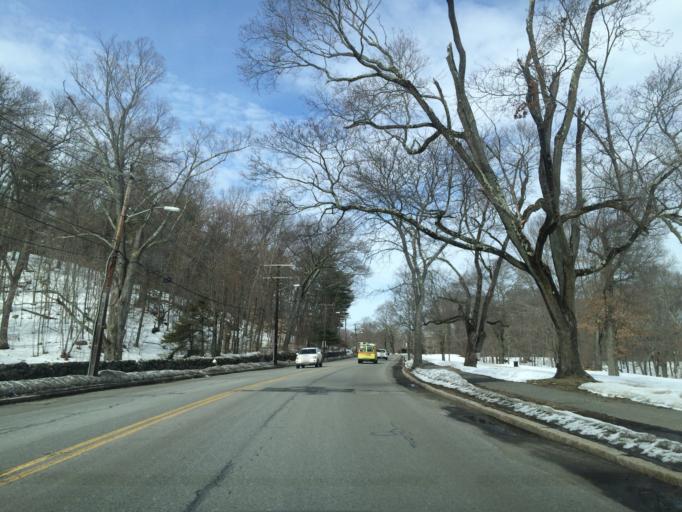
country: US
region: Massachusetts
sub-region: Middlesex County
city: Lexington
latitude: 42.4369
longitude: -71.2127
